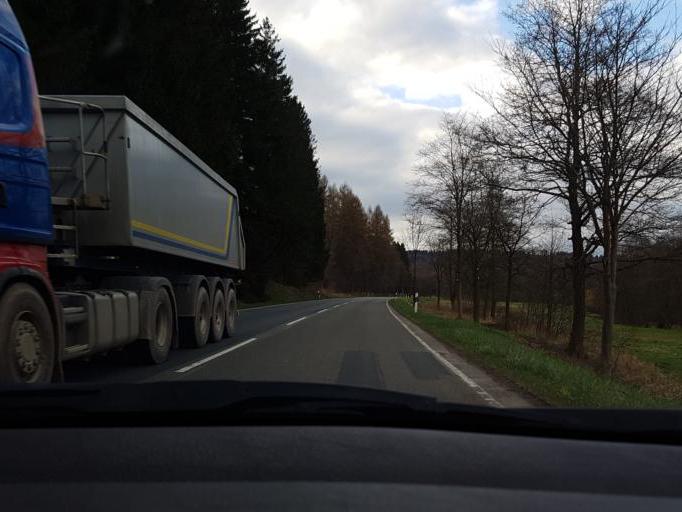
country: DE
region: Lower Saxony
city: Derental
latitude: 51.7223
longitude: 9.5184
